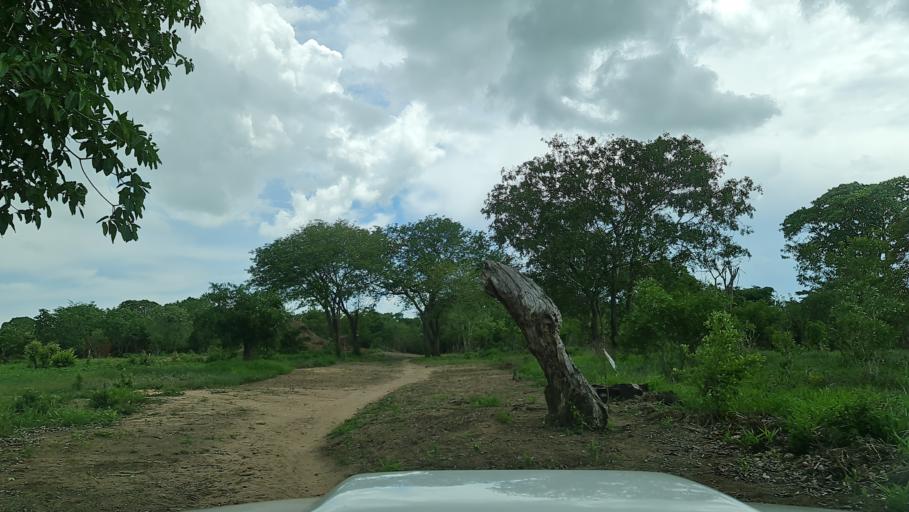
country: MZ
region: Nampula
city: Ilha de Mocambique
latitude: -15.5014
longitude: 40.1583
